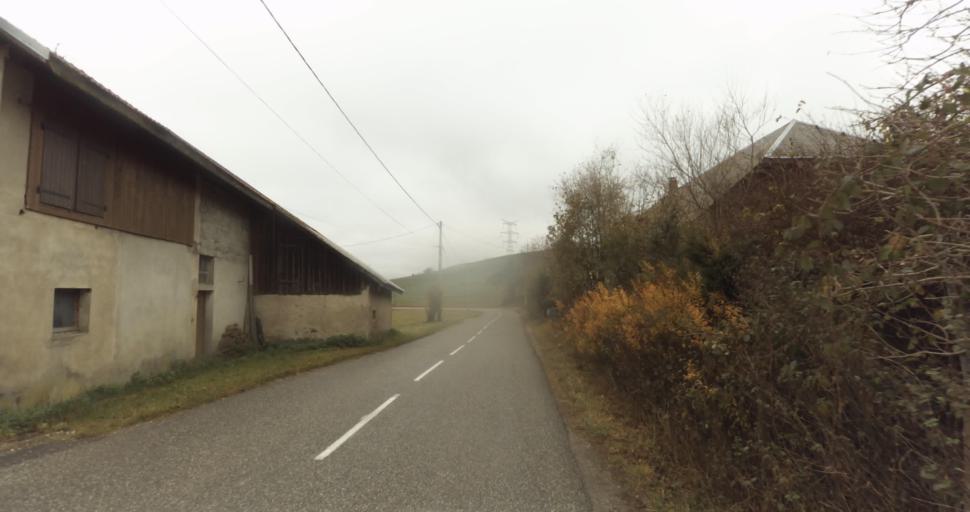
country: FR
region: Rhone-Alpes
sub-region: Departement de la Haute-Savoie
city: Evires
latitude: 46.0513
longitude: 6.2013
